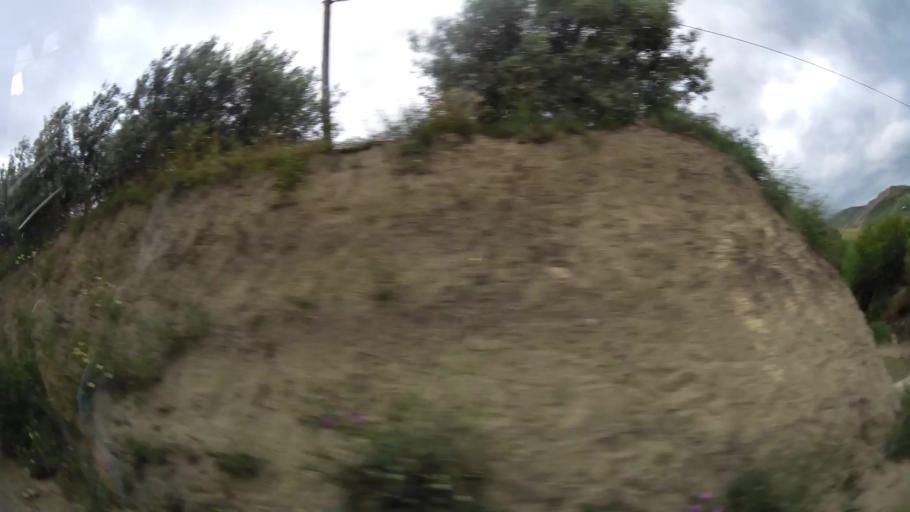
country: MA
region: Taza-Al Hoceima-Taounate
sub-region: Taza
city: Taza
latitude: 34.2941
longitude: -3.9684
